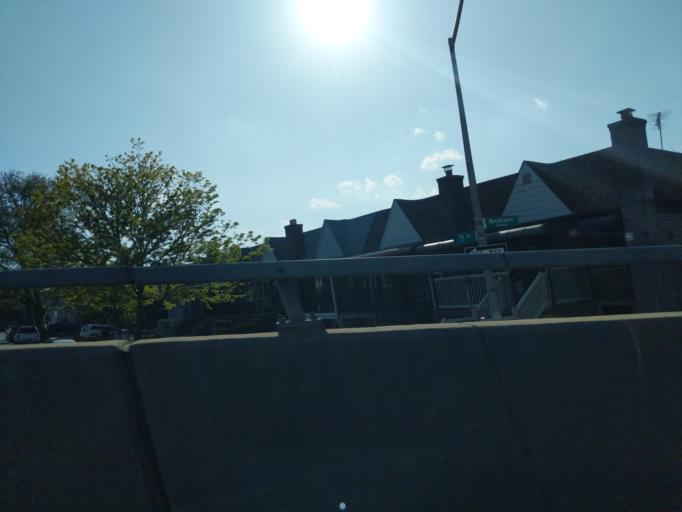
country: US
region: New York
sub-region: Queens County
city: Borough of Queens
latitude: 40.7093
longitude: -73.8596
